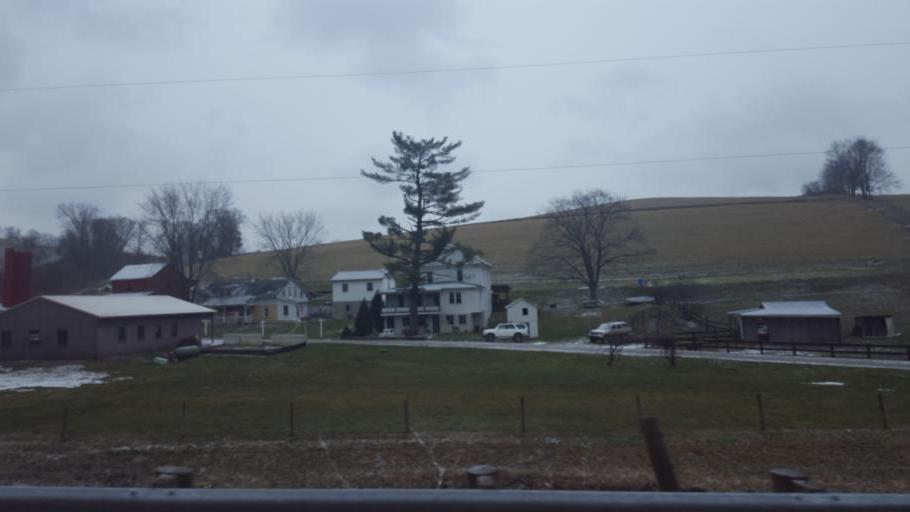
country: US
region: Ohio
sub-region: Coshocton County
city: West Lafayette
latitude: 40.4132
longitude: -81.7725
